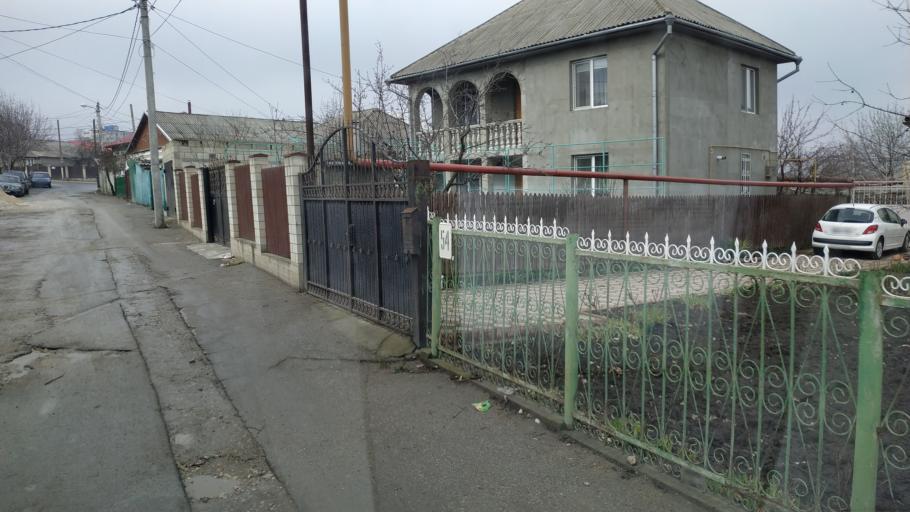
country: MD
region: Chisinau
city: Vatra
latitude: 47.0183
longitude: 28.7565
